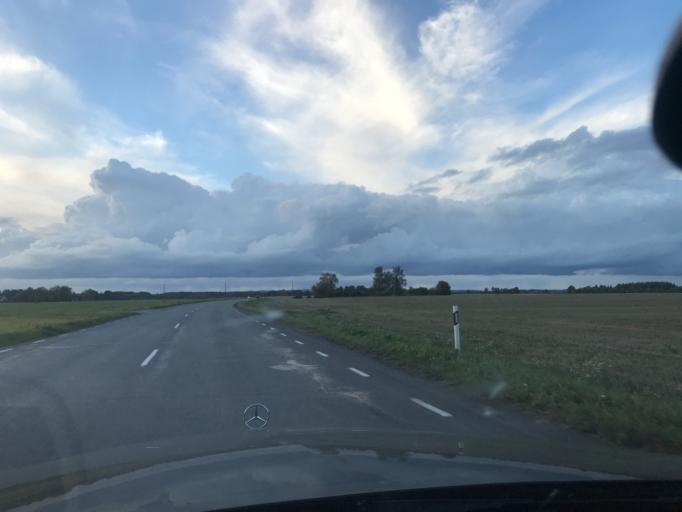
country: EE
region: Vorumaa
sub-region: Antsla vald
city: Vana-Antsla
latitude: 57.8974
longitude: 26.4833
